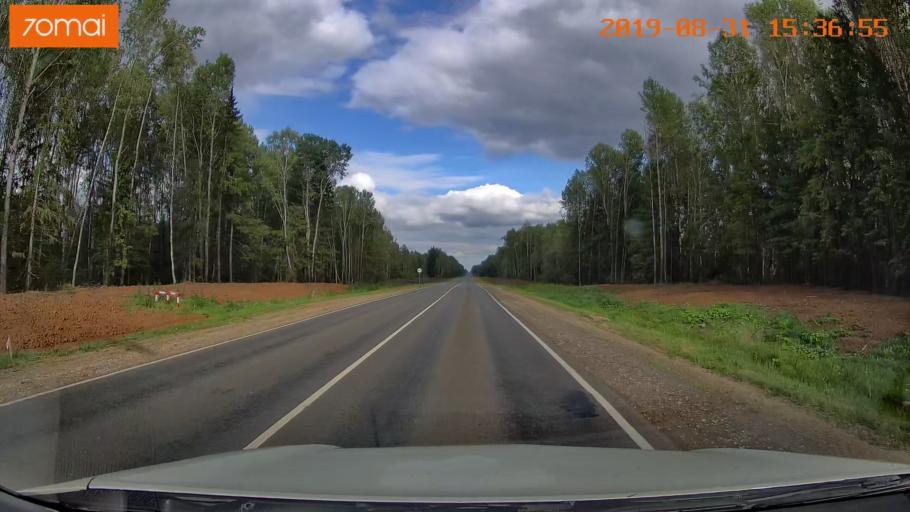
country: RU
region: Kaluga
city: Mosal'sk
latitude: 54.6146
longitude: 34.7712
